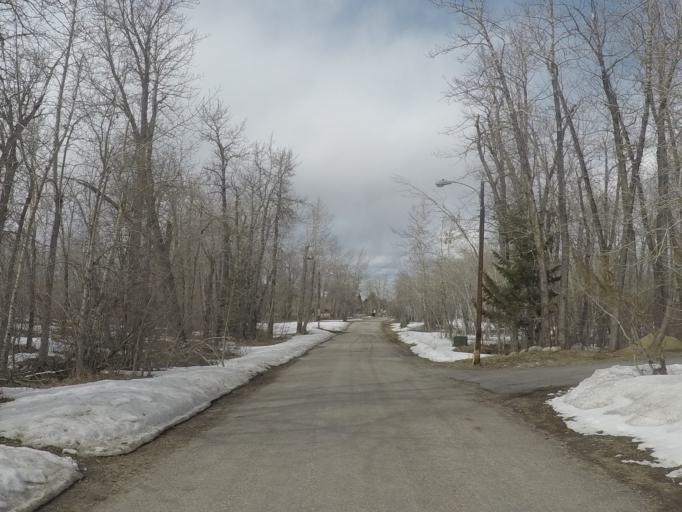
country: US
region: Montana
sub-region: Carbon County
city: Red Lodge
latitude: 45.1748
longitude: -109.2481
